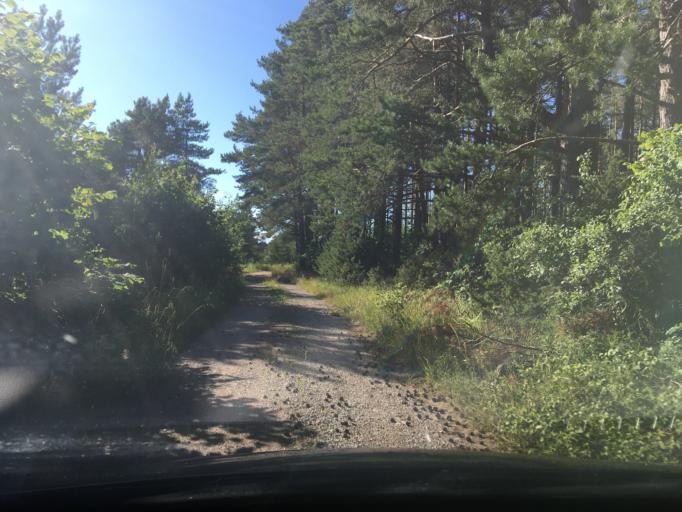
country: EE
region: Laeaene
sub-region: Lihula vald
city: Lihula
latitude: 58.5887
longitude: 23.7421
